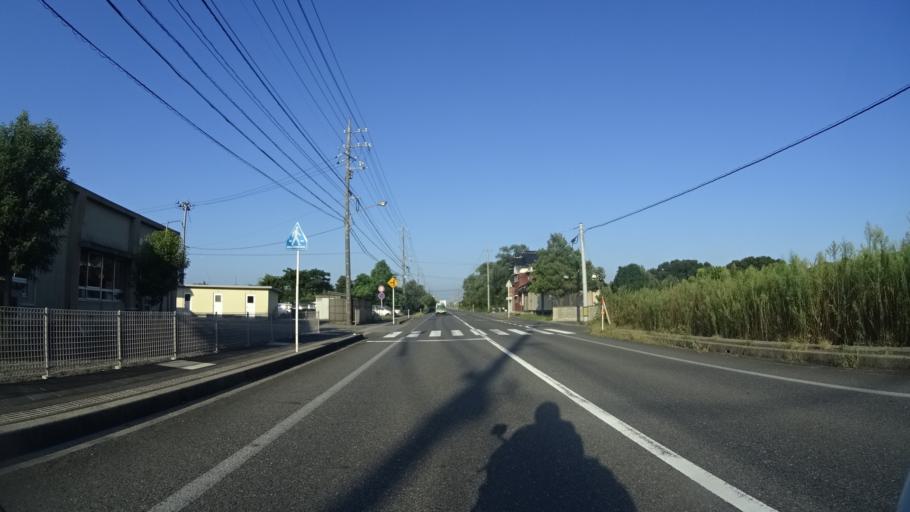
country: JP
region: Shimane
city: Sakaiminato
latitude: 35.5215
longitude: 133.2305
